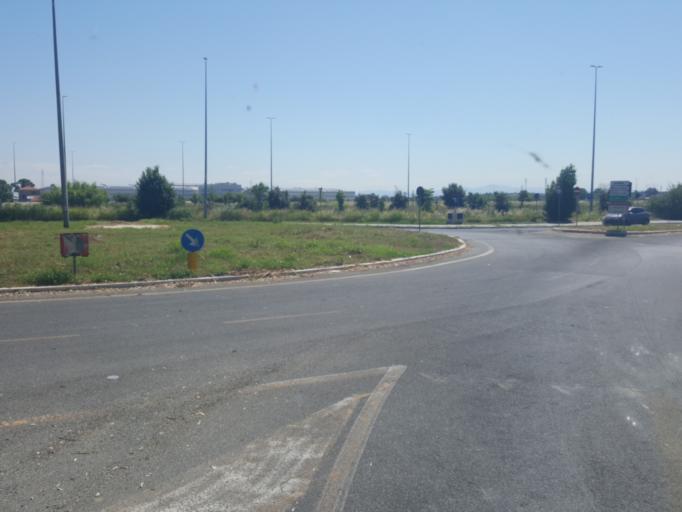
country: IT
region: Latium
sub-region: Citta metropolitana di Roma Capitale
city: Npp 23 (Parco Leonardo)
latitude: 41.8036
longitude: 12.3140
